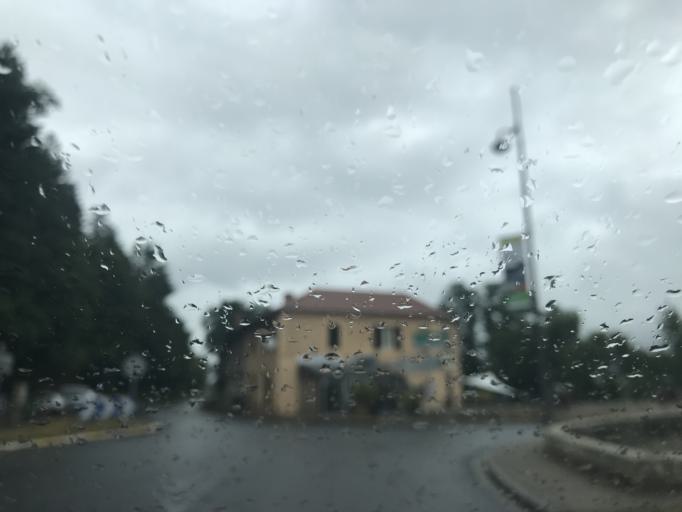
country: FR
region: Auvergne
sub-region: Departement du Puy-de-Dome
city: Ambert
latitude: 45.5504
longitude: 3.7301
